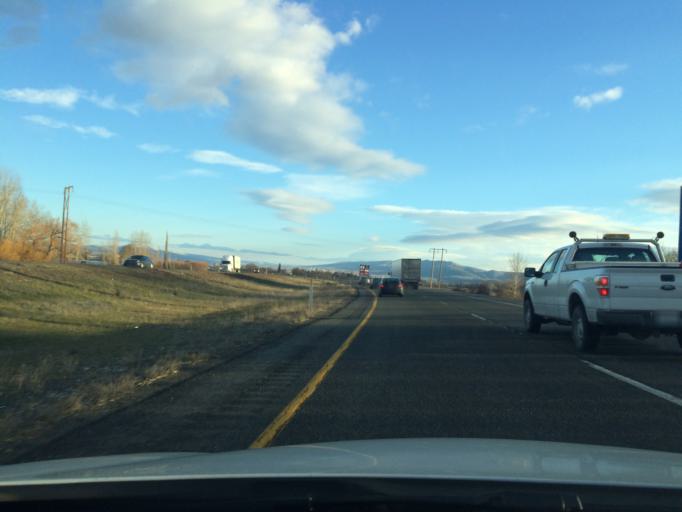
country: US
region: Washington
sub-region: Kittitas County
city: Ellensburg
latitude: 46.9779
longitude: -120.5568
